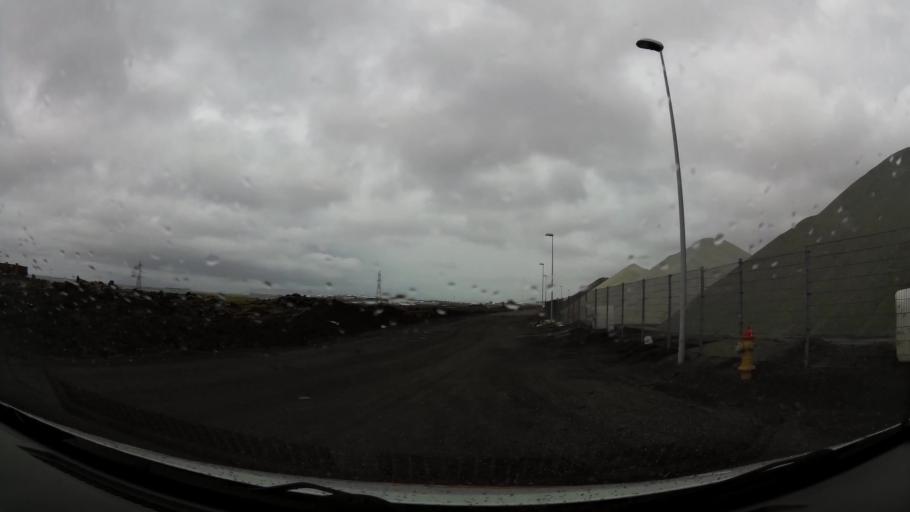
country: IS
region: Capital Region
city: Alftanes
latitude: 64.0398
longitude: -22.0128
